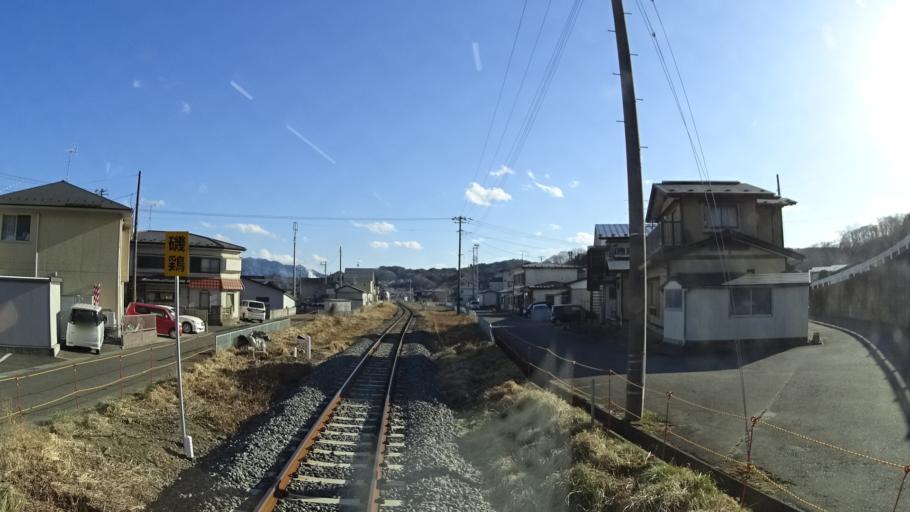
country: JP
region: Iwate
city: Miyako
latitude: 39.6320
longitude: 141.9614
